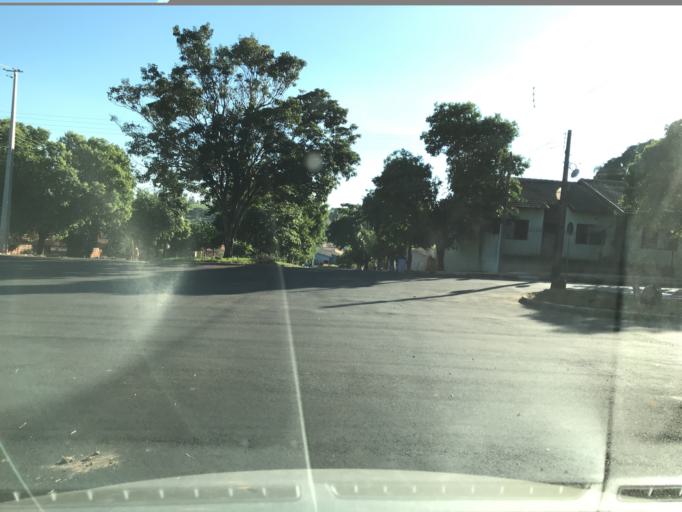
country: BR
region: Parana
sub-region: Ipora
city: Ipora
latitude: -23.9995
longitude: -53.7115
